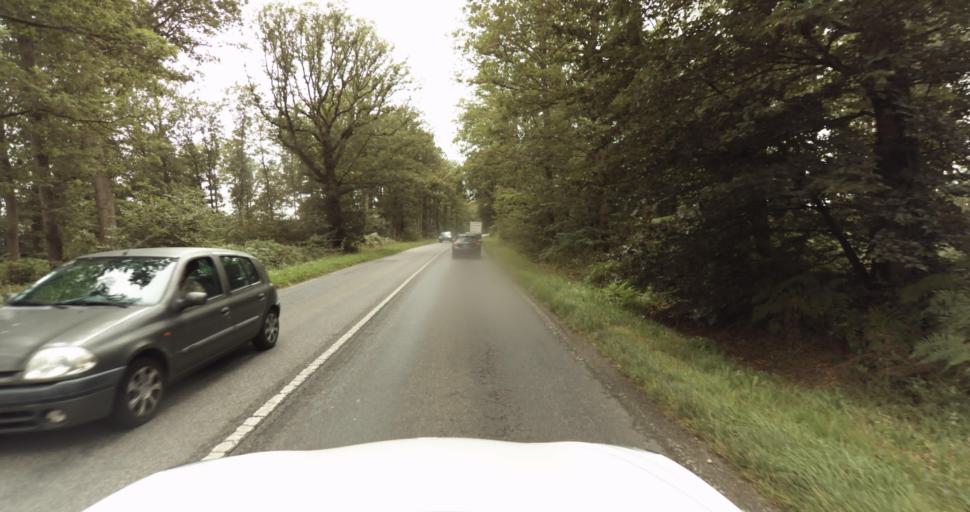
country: FR
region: Haute-Normandie
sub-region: Departement de l'Eure
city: Saint-Sebastien-de-Morsent
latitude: 49.0103
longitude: 1.0982
